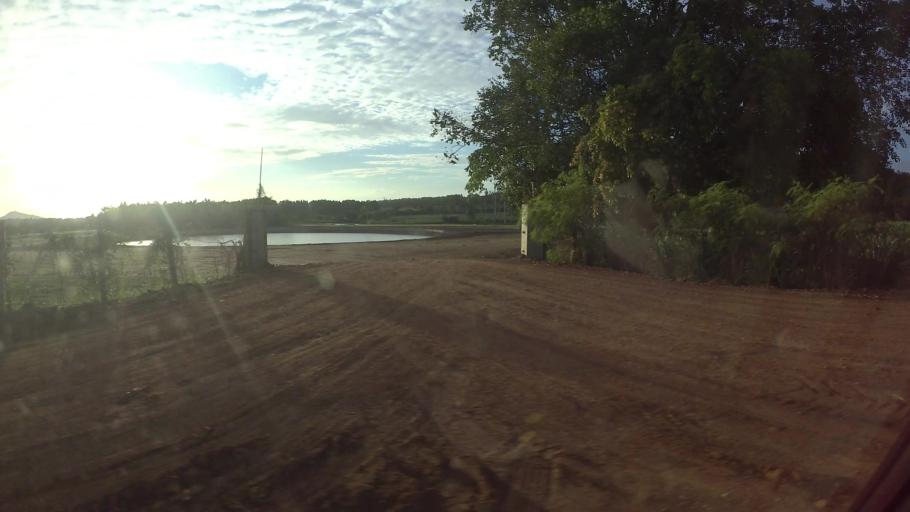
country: TH
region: Chon Buri
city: Sattahip
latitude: 12.7516
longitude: 100.9424
